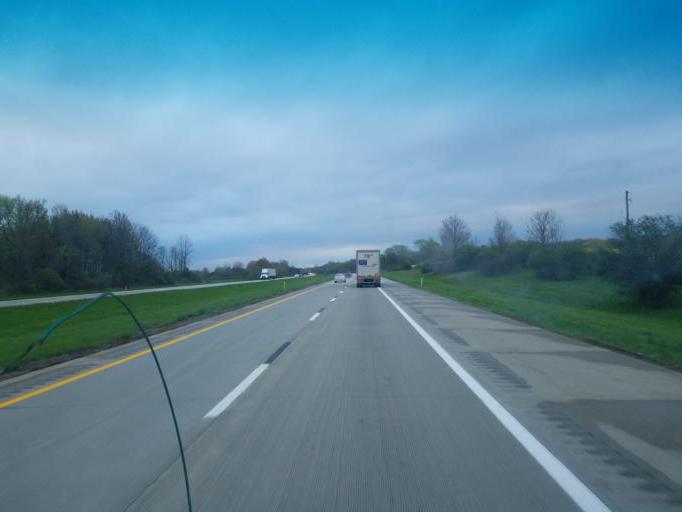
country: US
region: Ohio
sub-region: Lake County
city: Perry
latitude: 41.7195
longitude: -81.1386
